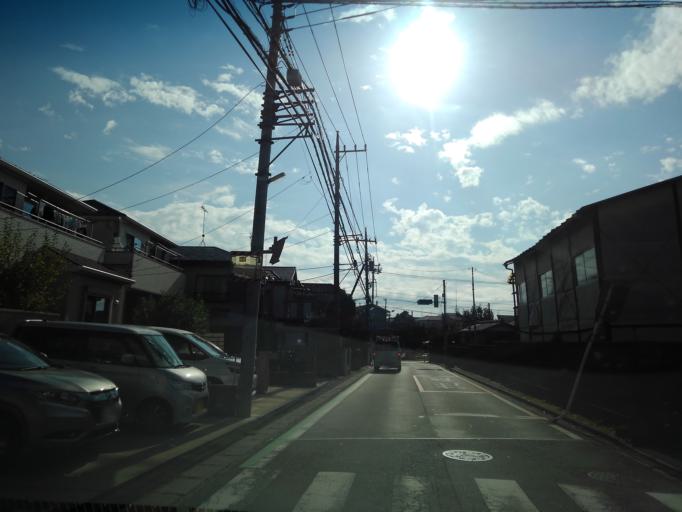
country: JP
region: Saitama
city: Tokorozawa
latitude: 35.7785
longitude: 139.4693
